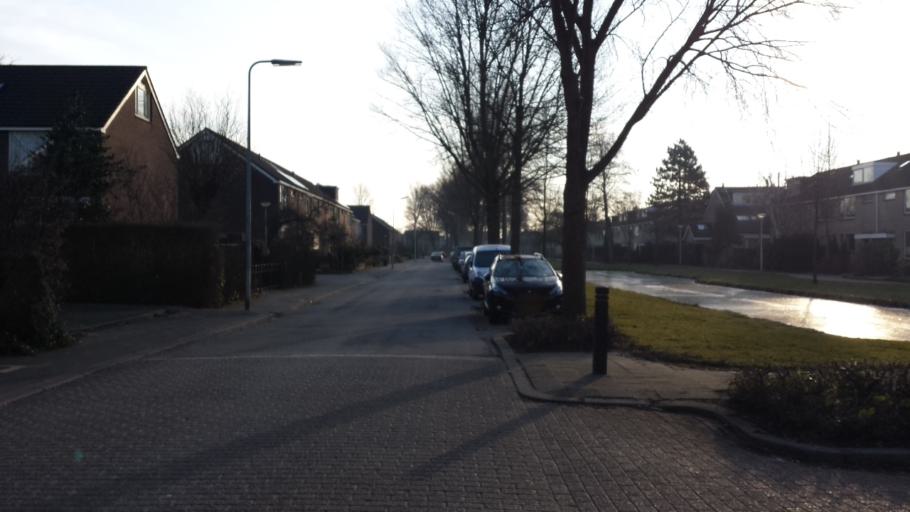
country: NL
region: South Holland
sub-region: Gemeente Gouda
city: Gouda
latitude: 52.0299
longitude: 4.7091
